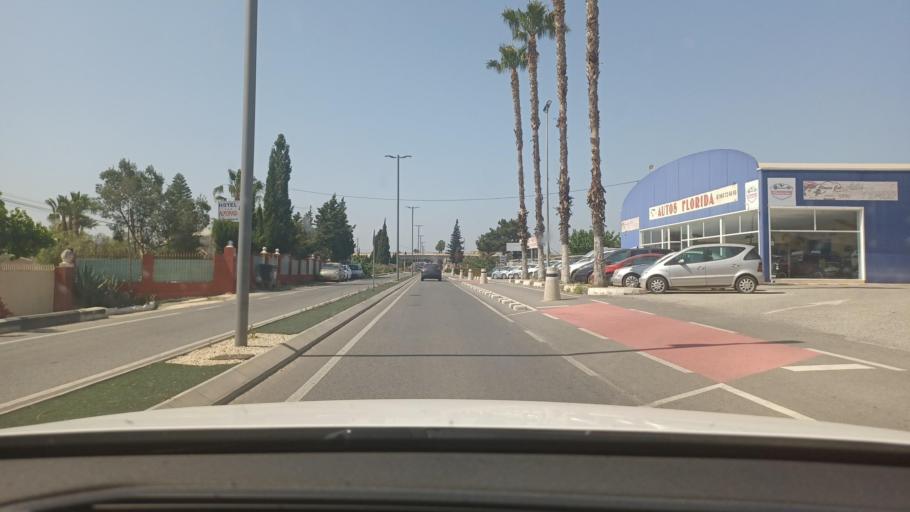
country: ES
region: Valencia
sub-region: Provincia de Alicante
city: Dolores
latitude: 38.1283
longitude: -0.7783
